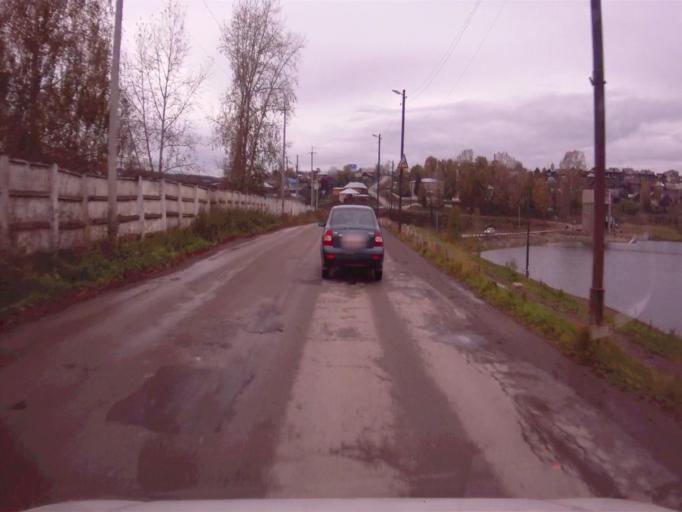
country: RU
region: Chelyabinsk
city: Nyazepetrovsk
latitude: 56.0549
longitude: 59.5924
